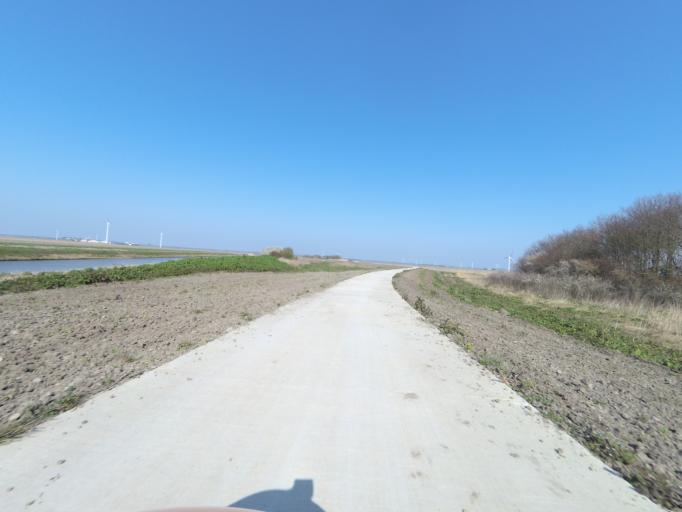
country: NL
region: Utrecht
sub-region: Gemeente Bunschoten
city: Spakenburg
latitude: 52.3688
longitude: 5.3776
